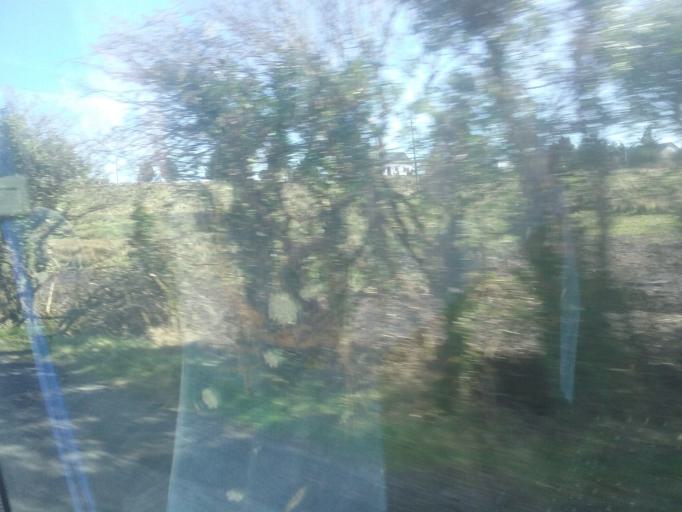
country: IE
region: Connaught
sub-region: County Galway
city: Bearna
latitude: 53.0218
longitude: -9.2694
